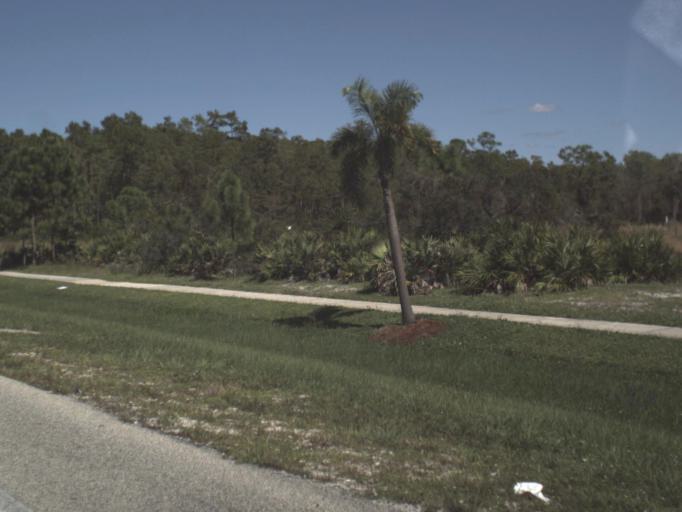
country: US
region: Florida
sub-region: Lee County
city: Bonita Springs
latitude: 26.3073
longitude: -81.8045
